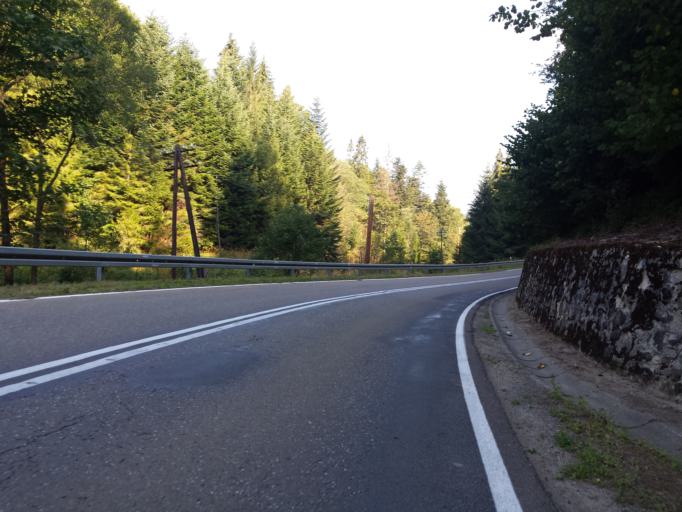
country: PL
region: Subcarpathian Voivodeship
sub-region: Powiat leski
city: Cisna
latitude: 49.2288
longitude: 22.3033
